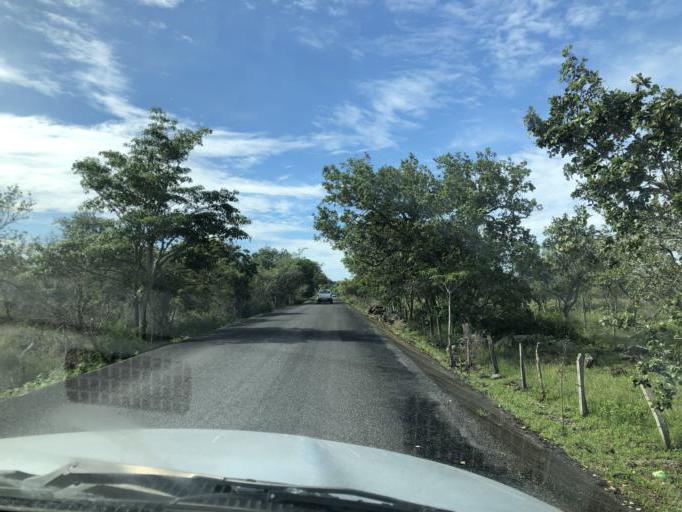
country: MX
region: Veracruz
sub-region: Alto Lucero de Gutierrez Barrios
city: Palma Sola
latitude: 19.7892
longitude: -96.5528
